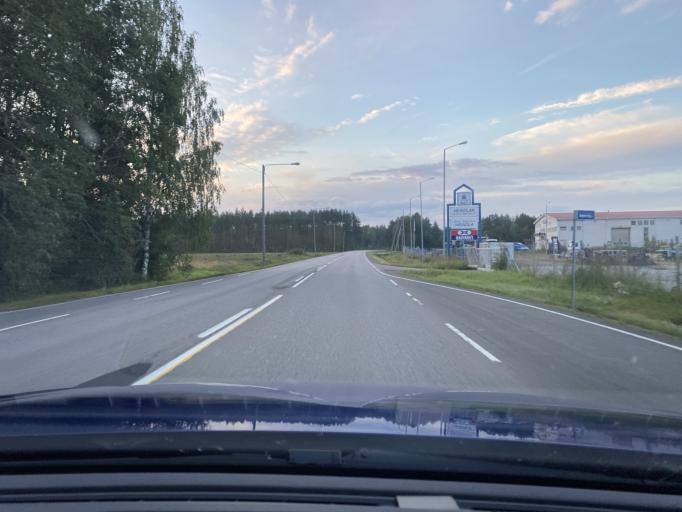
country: FI
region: Satakunta
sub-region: Pohjois-Satakunta
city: Honkajoki
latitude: 61.9684
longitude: 22.2214
